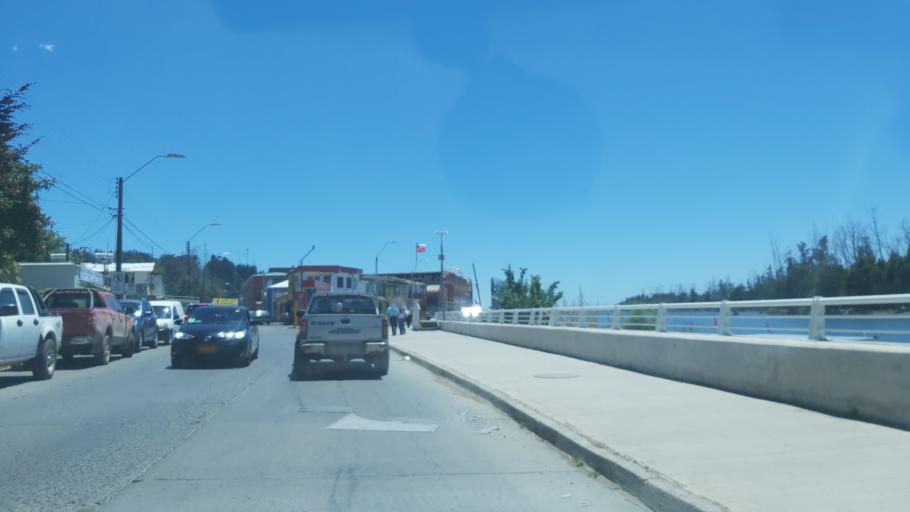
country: CL
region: Maule
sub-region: Provincia de Talca
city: Constitucion
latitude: -35.3325
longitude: -72.4061
